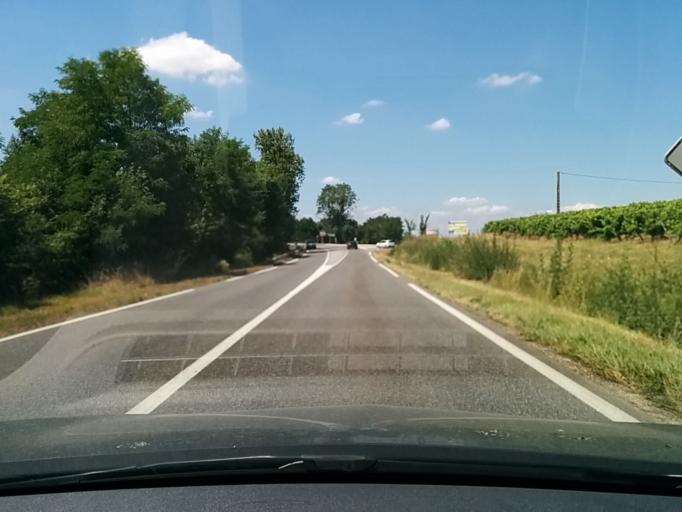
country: FR
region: Midi-Pyrenees
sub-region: Departement du Gers
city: Eauze
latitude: 43.7914
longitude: 0.1026
